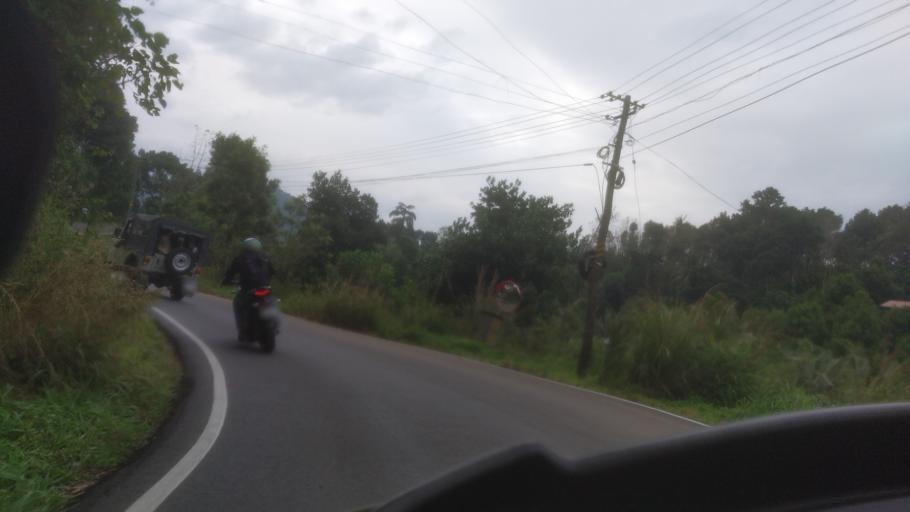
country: IN
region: Kerala
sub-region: Idukki
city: Idukki
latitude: 9.9423
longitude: 77.0220
